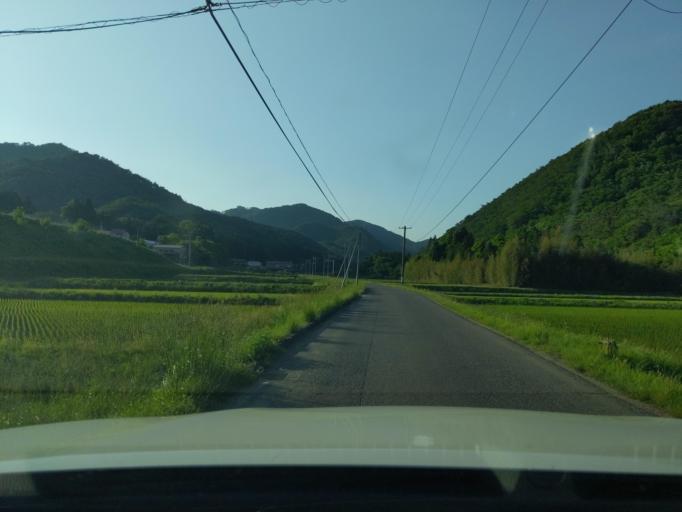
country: JP
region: Fukushima
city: Motomiya
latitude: 37.4944
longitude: 140.3280
